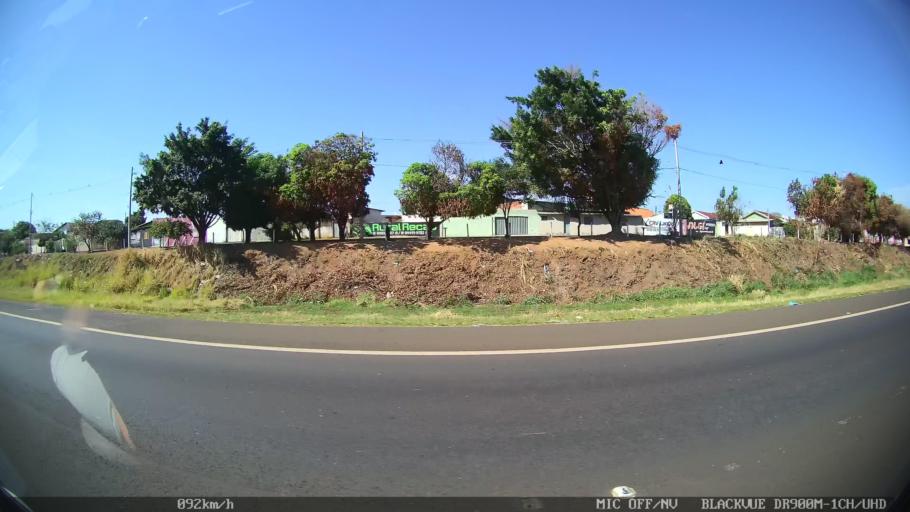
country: BR
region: Sao Paulo
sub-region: Franca
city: Franca
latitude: -20.5245
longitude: -47.4201
